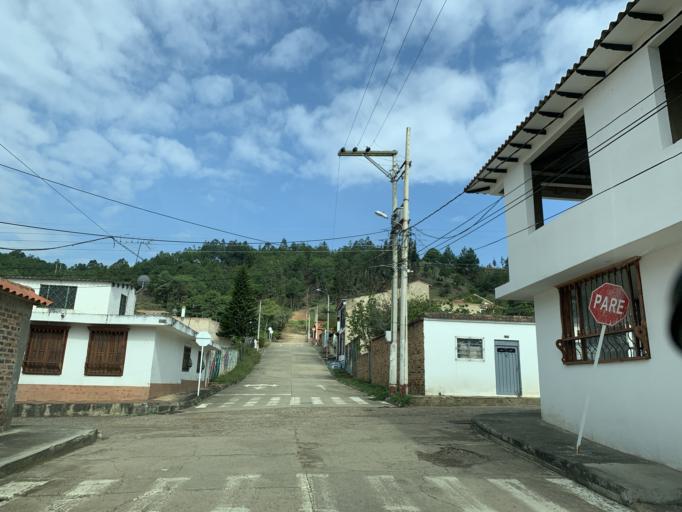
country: CO
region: Boyaca
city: Raquira
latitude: 5.5807
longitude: -73.6468
